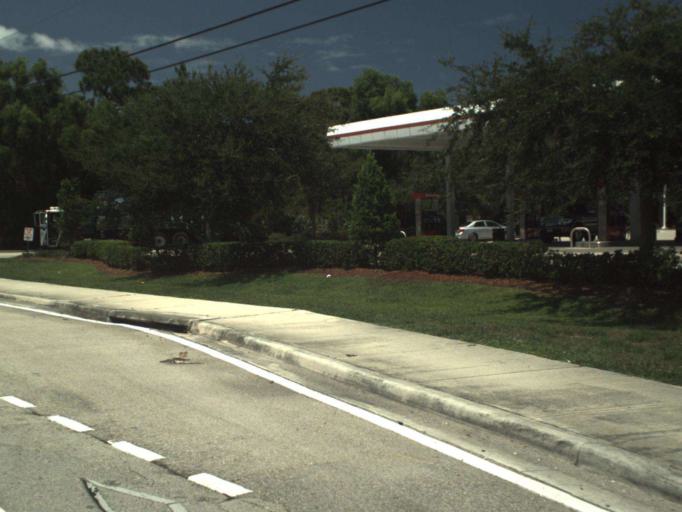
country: US
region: Florida
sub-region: Saint Lucie County
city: River Park
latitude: 27.3120
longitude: -80.3121
